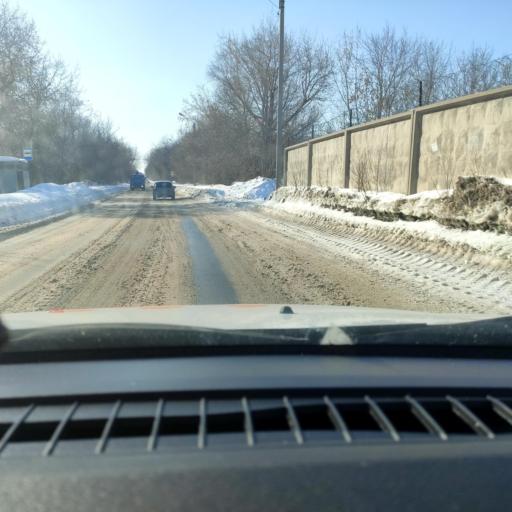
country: RU
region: Samara
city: Novokuybyshevsk
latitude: 53.1190
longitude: 49.9116
